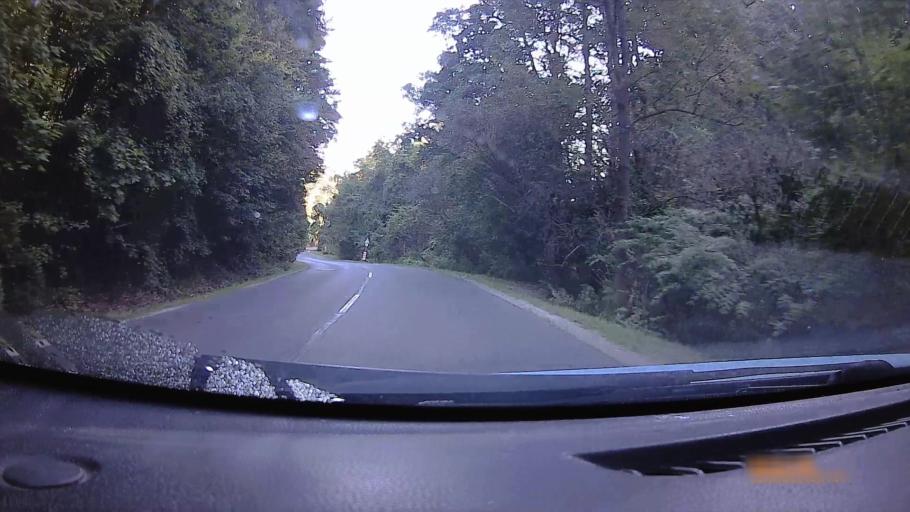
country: HU
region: Borsod-Abauj-Zemplen
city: Sajobabony
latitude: 48.1123
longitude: 20.6508
